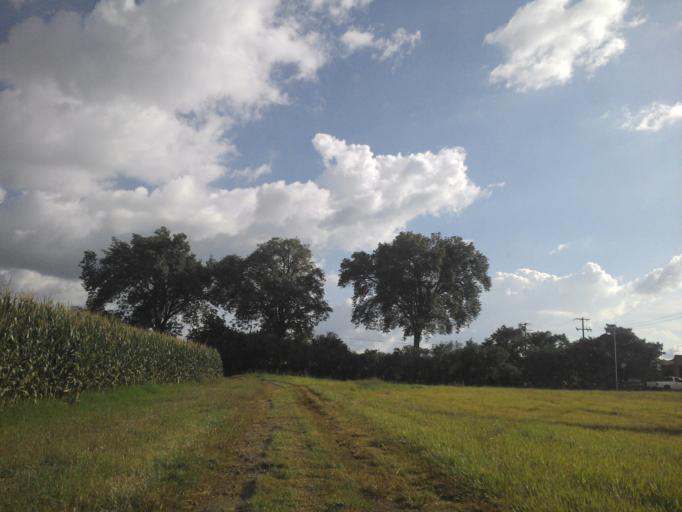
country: MX
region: Jalisco
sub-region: Atotonilco el Alto
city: Ojo de Agua de Moran
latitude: 20.6079
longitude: -102.4709
